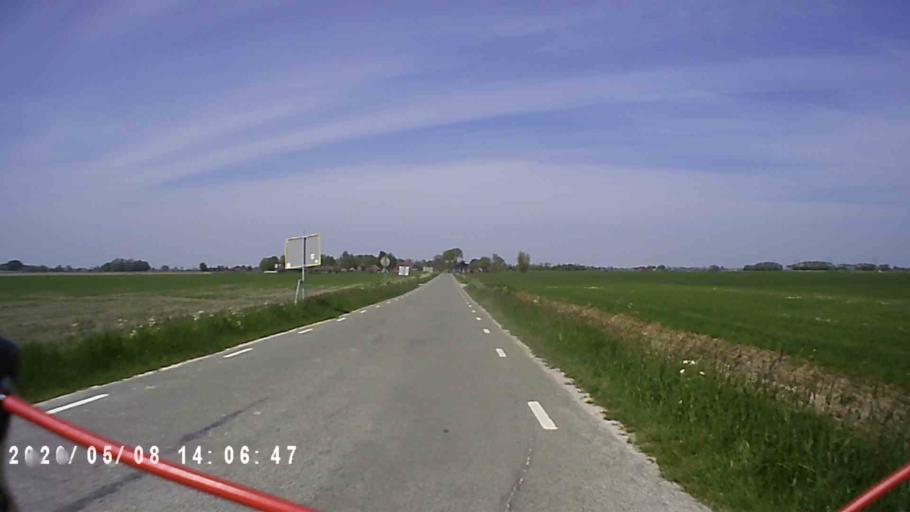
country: NL
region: Groningen
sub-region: Gemeente Appingedam
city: Appingedam
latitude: 53.3361
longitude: 6.8027
